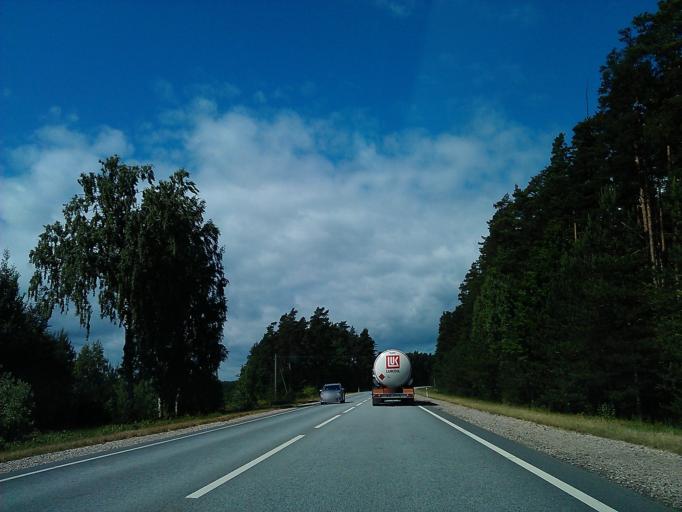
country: LV
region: Jurmala
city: Jurmala
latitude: 56.9272
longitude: 23.6706
